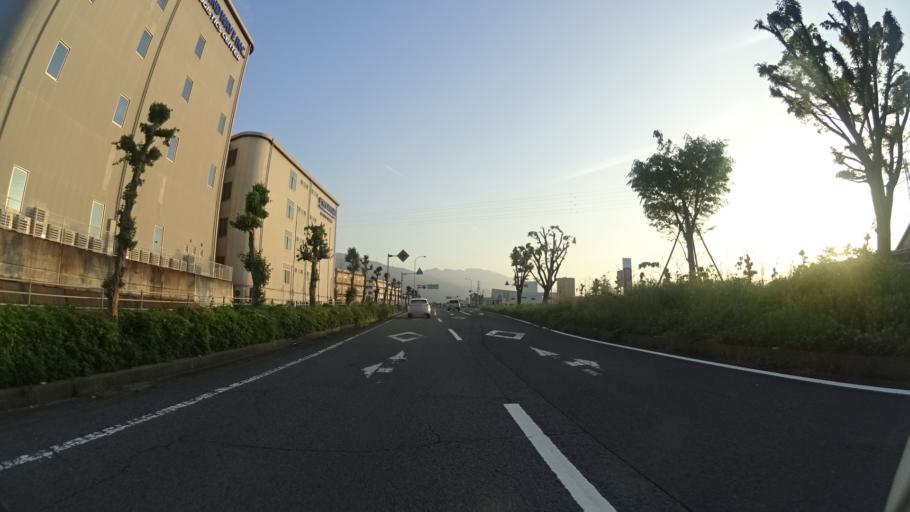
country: JP
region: Ehime
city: Kawanoecho
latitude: 33.9891
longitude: 133.5794
